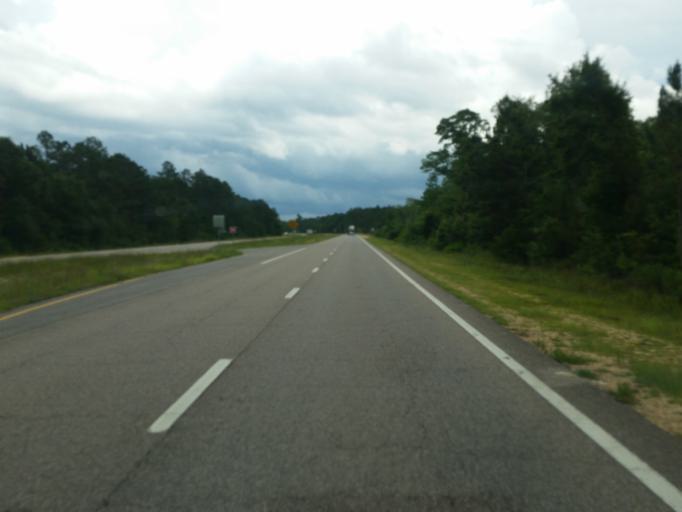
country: US
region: Mississippi
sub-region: George County
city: Lucedale
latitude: 30.8698
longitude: -88.4271
